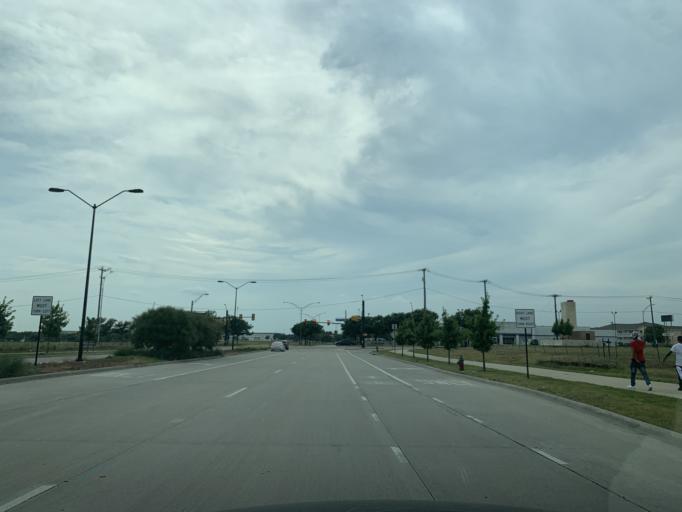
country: US
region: Texas
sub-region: Tarrant County
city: Haltom City
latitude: 32.8349
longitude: -97.2891
